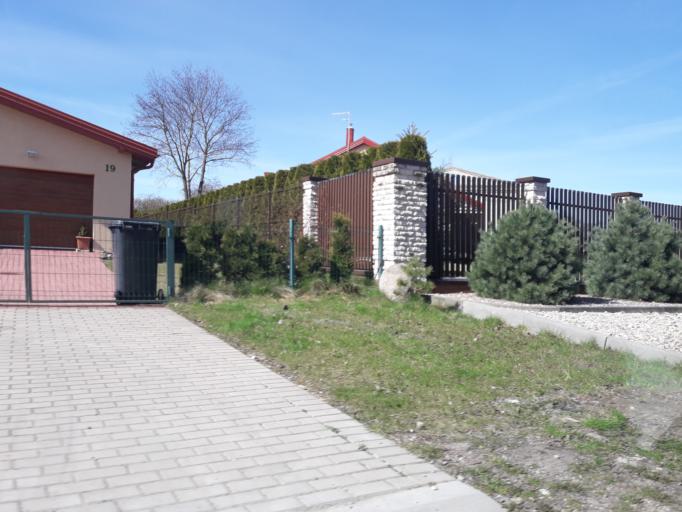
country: LT
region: Siauliu apskritis
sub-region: Siauliai
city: Siauliai
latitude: 55.9424
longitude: 23.3181
